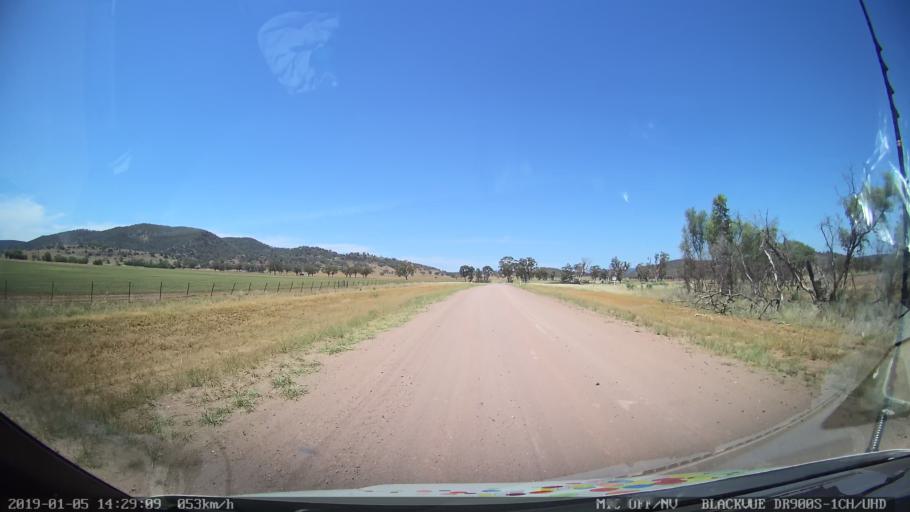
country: AU
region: New South Wales
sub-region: Tamworth Municipality
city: Phillip
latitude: -31.2300
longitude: 150.5793
